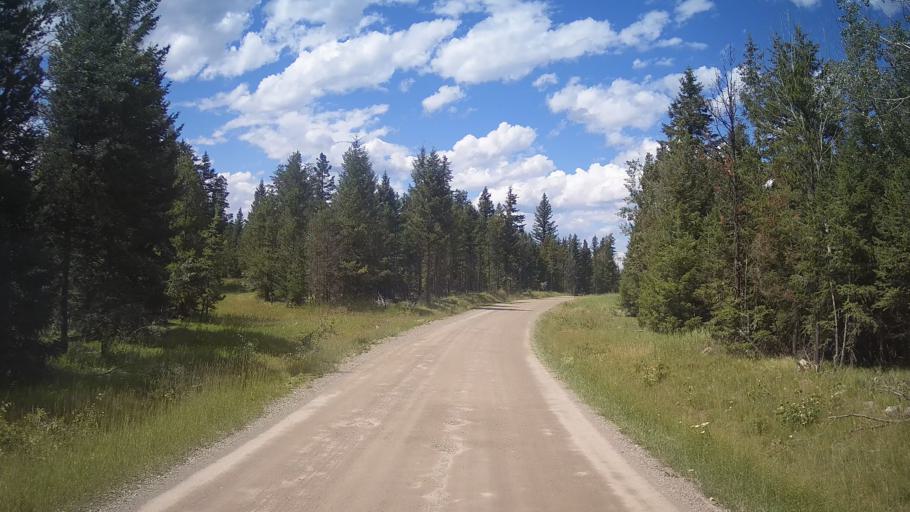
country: CA
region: British Columbia
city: Lillooet
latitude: 51.3170
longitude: -121.8597
